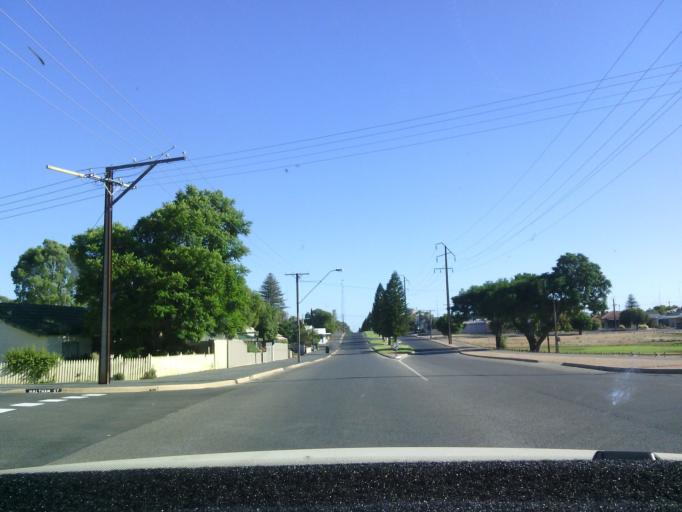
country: AU
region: South Australia
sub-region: Berri and Barmera
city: Berri
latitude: -34.2803
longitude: 140.5974
